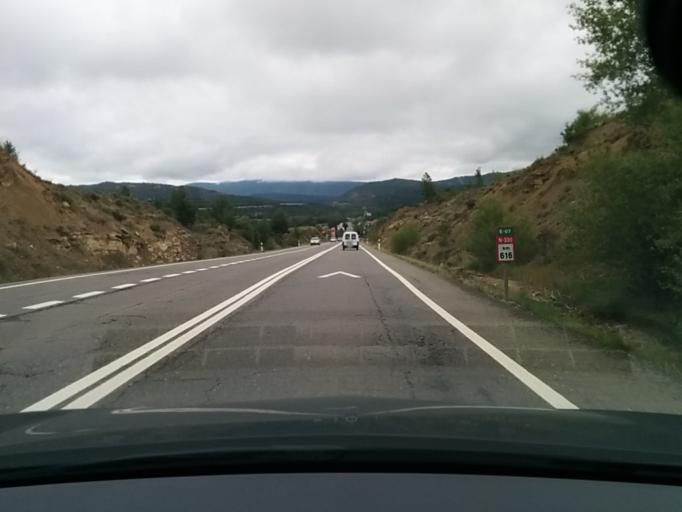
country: ES
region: Aragon
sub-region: Provincia de Huesca
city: Sabinanigo
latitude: 42.4311
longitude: -0.3979
